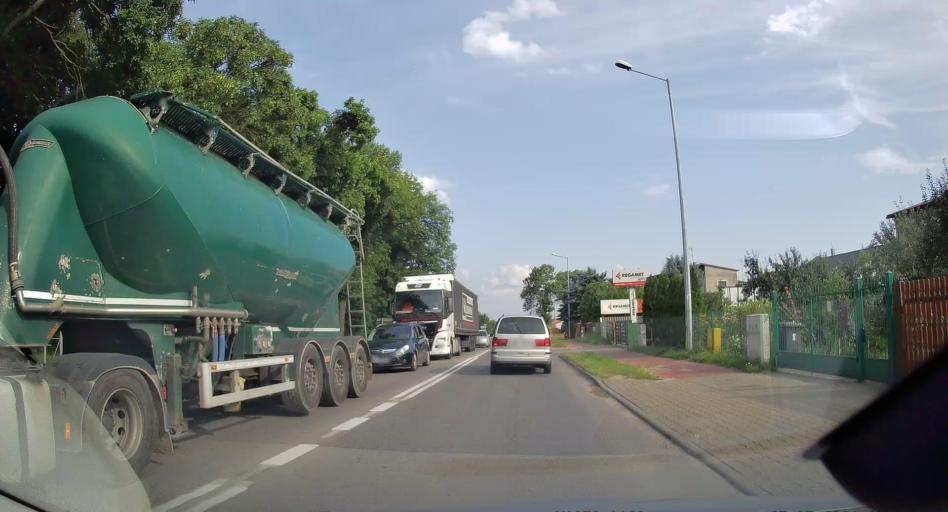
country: PL
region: Lodz Voivodeship
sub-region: Powiat opoczynski
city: Opoczno
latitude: 51.3684
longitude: 20.2964
